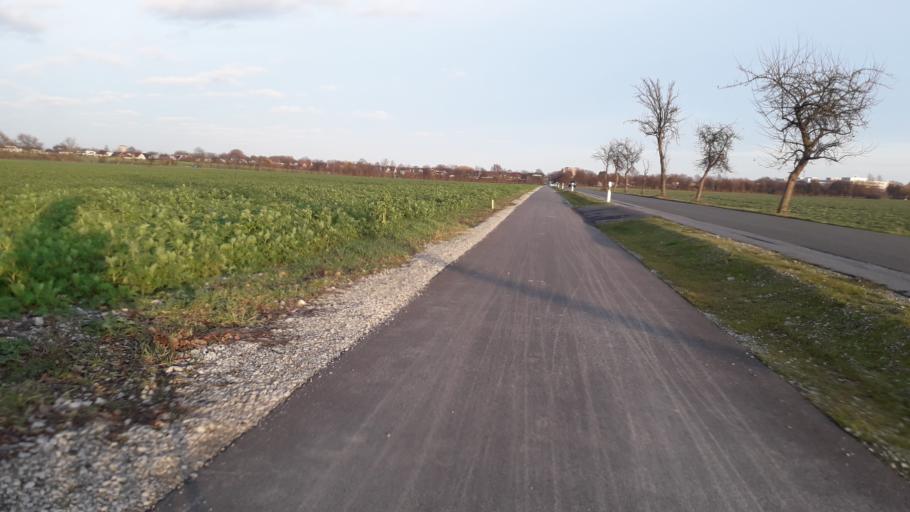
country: DE
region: North Rhine-Westphalia
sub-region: Regierungsbezirk Arnsberg
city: Soest
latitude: 51.5664
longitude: 8.0617
